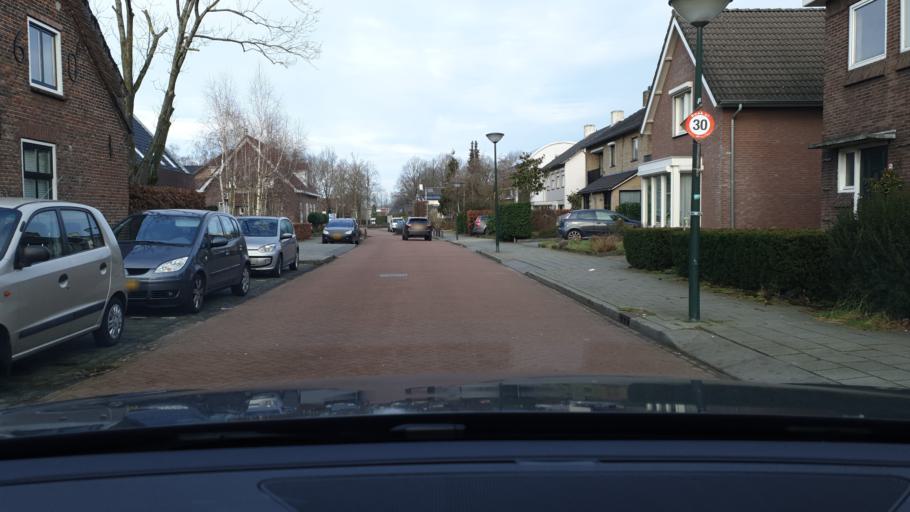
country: NL
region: North Brabant
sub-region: Gemeente Geldrop-Mierlo
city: Geldrop
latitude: 51.4274
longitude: 5.5454
